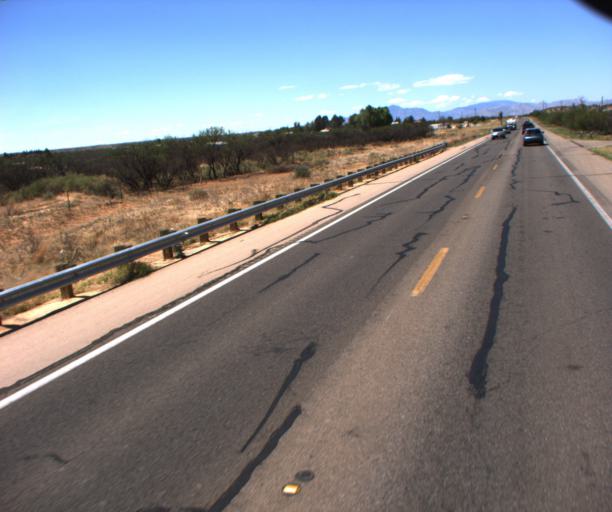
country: US
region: Arizona
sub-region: Cochise County
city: Saint David
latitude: 31.9139
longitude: -110.2611
